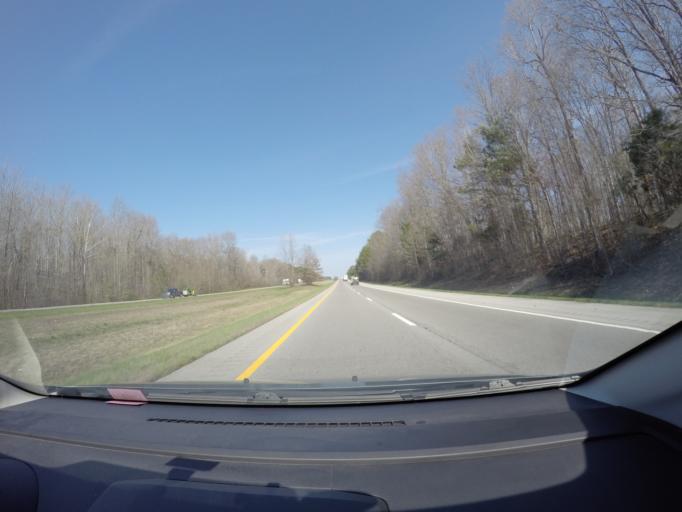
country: US
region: Tennessee
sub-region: Coffee County
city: Manchester
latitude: 35.4063
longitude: -86.0048
